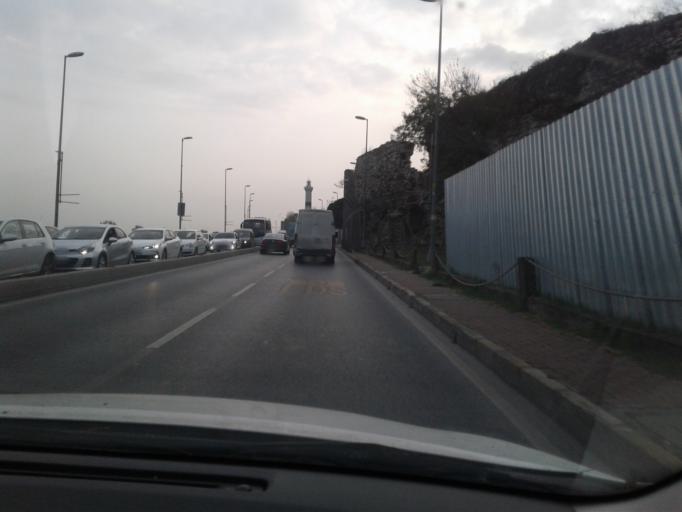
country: TR
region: Istanbul
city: Eminoenue
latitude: 41.0095
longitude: 28.9871
